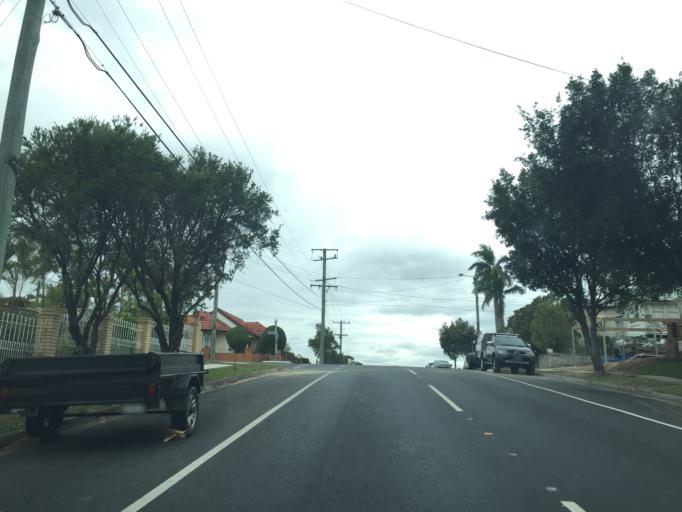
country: AU
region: Queensland
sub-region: Brisbane
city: Everton Park
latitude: -27.4380
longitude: 152.9828
